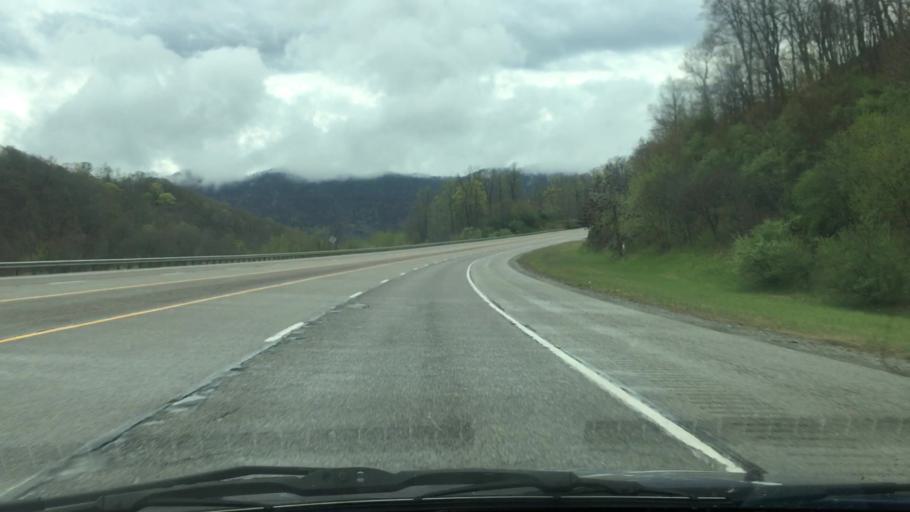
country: US
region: Kentucky
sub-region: Letcher County
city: Jenkins
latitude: 37.2027
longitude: -82.6226
